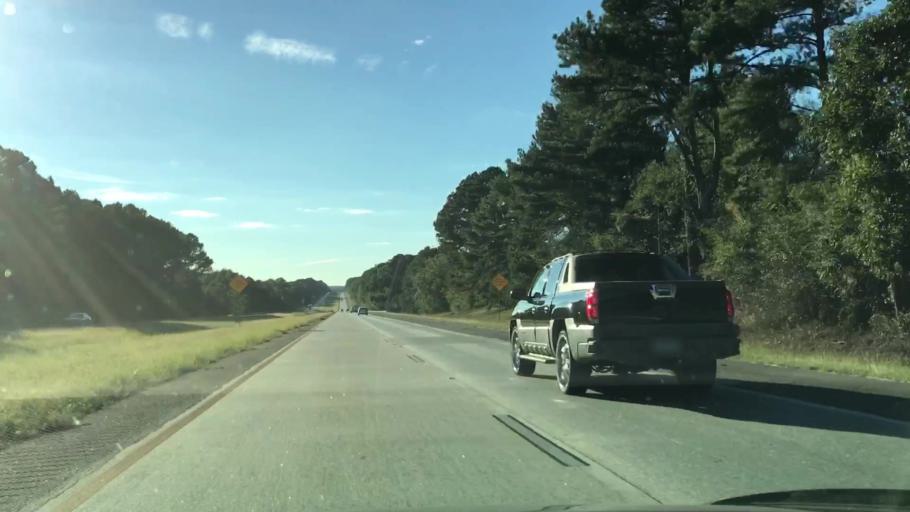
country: US
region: Georgia
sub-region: Greene County
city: Union Point
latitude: 33.5455
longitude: -83.0930
